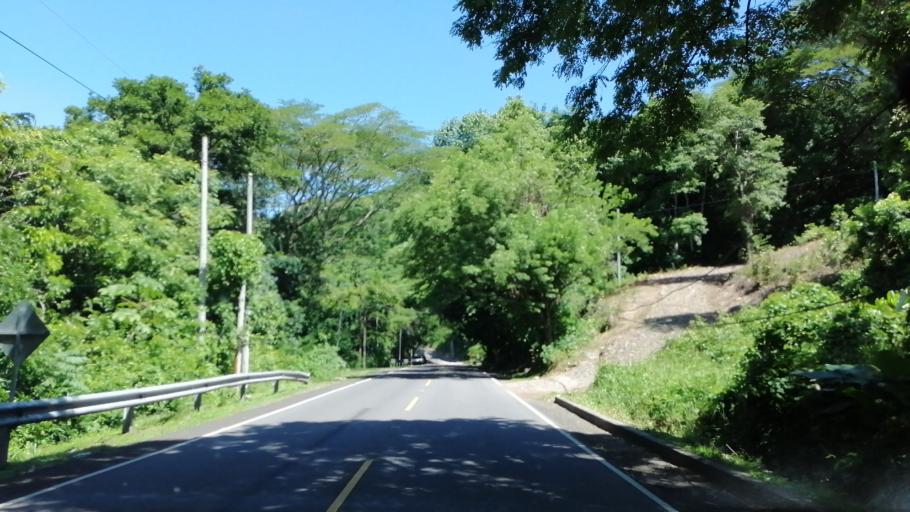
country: SV
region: Morazan
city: Cacaopera
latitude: 13.7941
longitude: -88.1479
